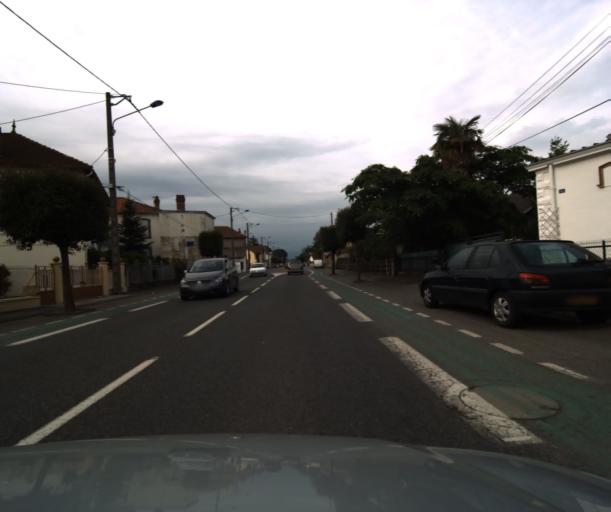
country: FR
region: Midi-Pyrenees
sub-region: Departement des Hautes-Pyrenees
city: Aureilhan
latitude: 43.2406
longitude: 0.0947
